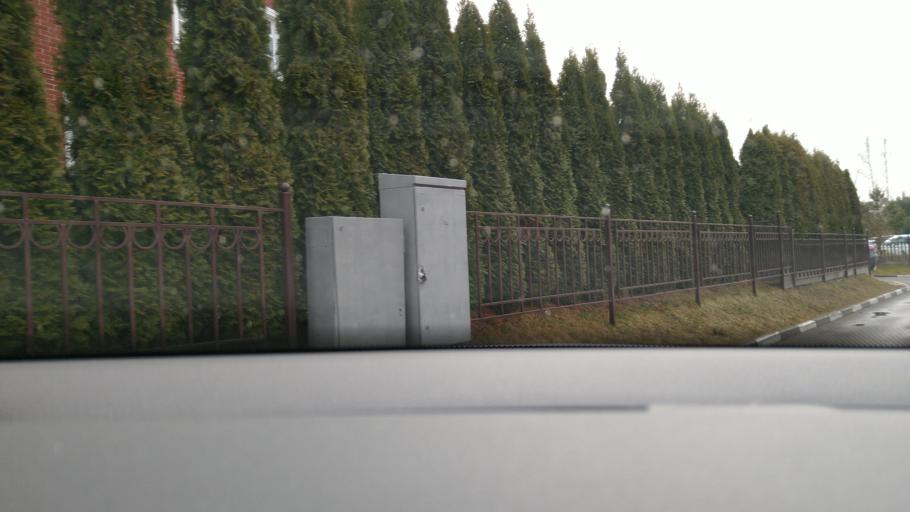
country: RU
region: Moskovskaya
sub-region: Leninskiy Rayon
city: Vnukovo
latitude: 55.6143
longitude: 37.3248
